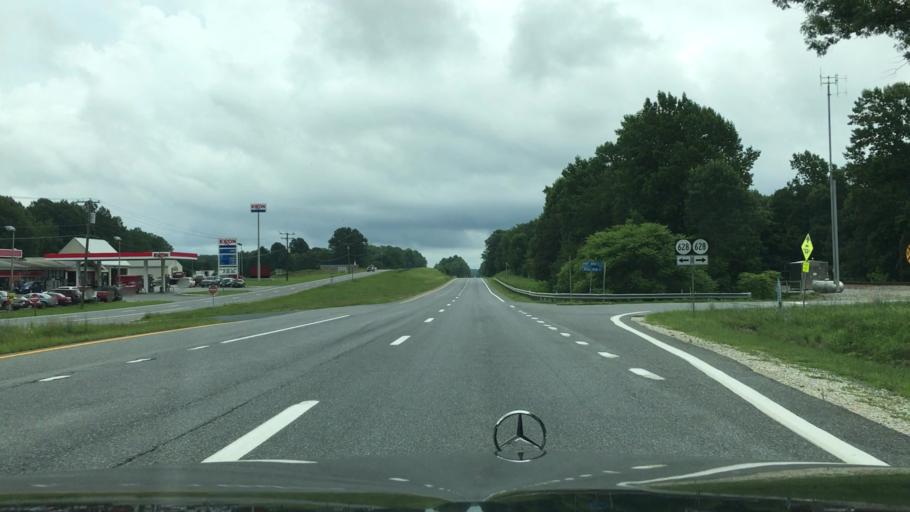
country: US
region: Virginia
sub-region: Appomattox County
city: Appomattox
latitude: 37.2789
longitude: -78.6977
